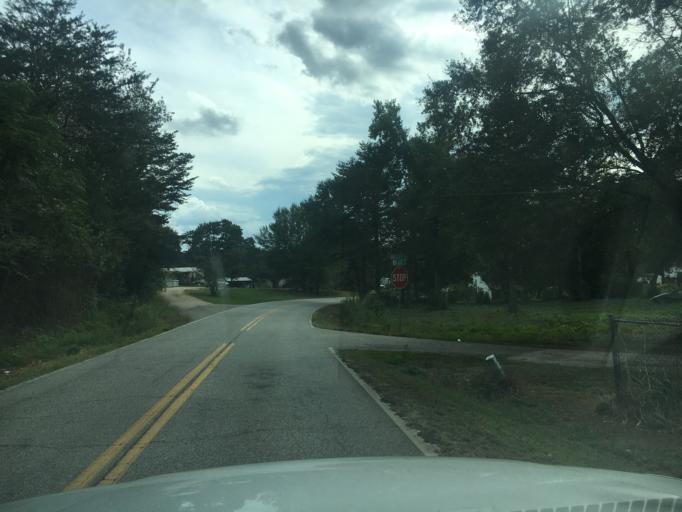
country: US
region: South Carolina
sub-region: Spartanburg County
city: Fairforest
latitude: 34.9020
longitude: -82.0534
